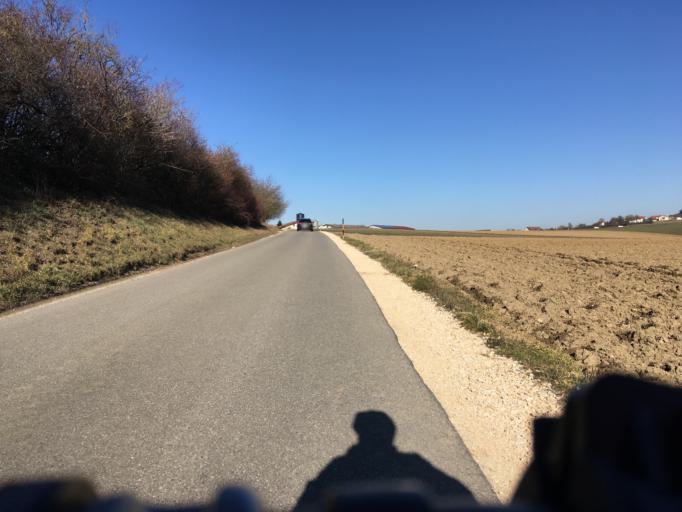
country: DE
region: Baden-Wuerttemberg
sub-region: Freiburg Region
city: Gottmadingen
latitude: 47.7462
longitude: 8.7436
